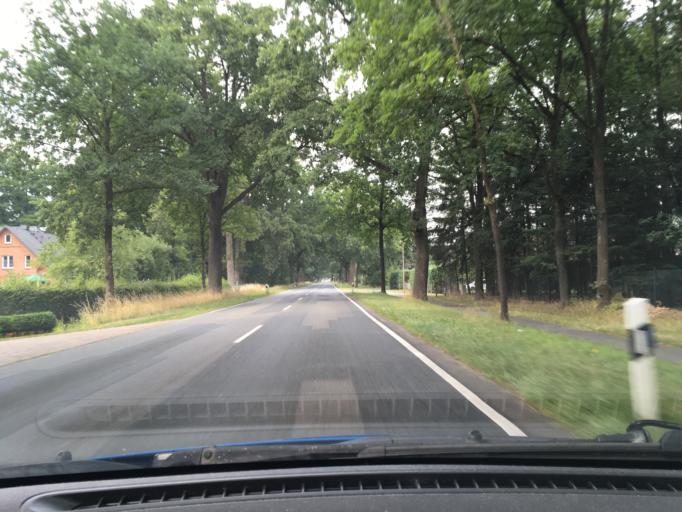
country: DE
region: Lower Saxony
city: Adelheidsdorf
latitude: 52.5763
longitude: 10.0634
